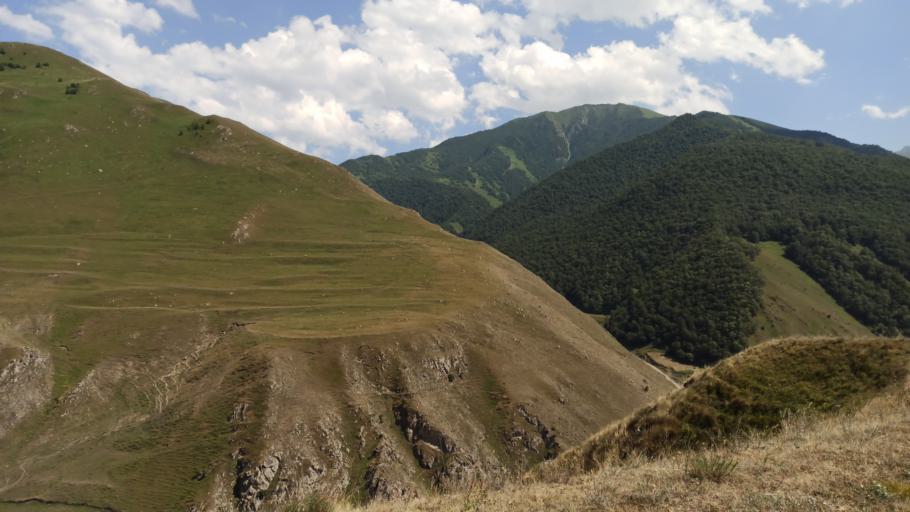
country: RU
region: Kabardino-Balkariya
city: Tyrnyauz
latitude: 43.3900
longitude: 42.9272
